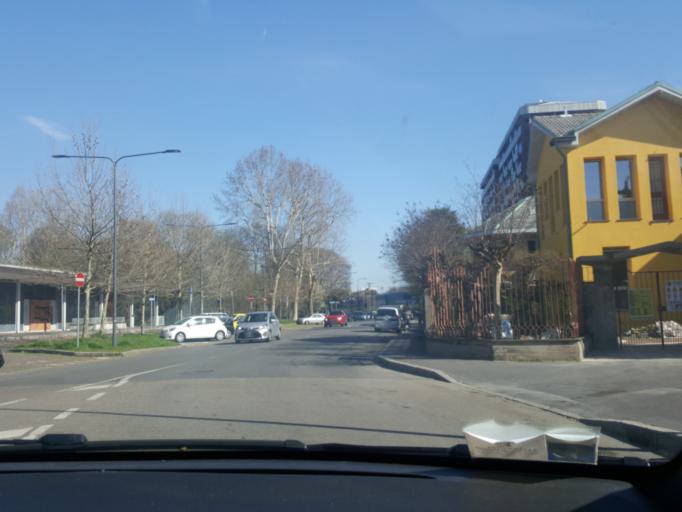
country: IT
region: Lombardy
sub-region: Citta metropolitana di Milano
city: Novate Milanese
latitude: 45.4866
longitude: 9.1371
